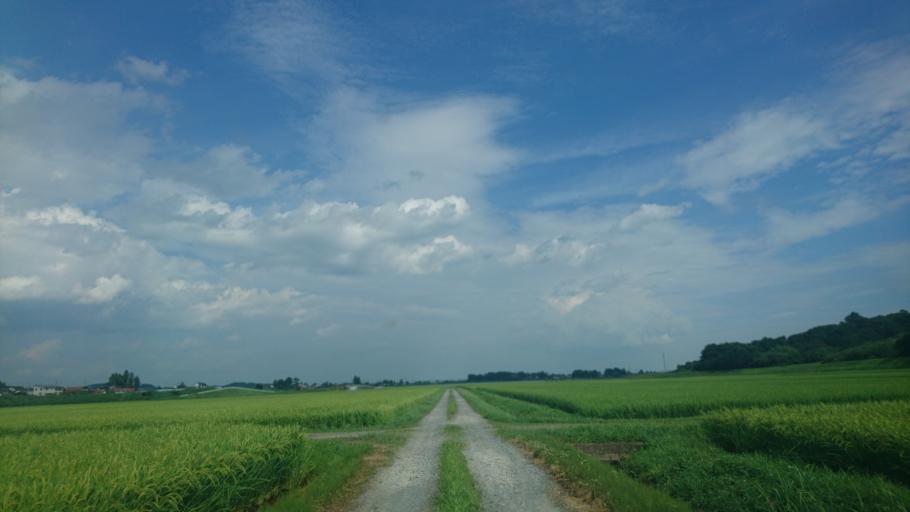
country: JP
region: Iwate
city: Ichinoseki
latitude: 38.7721
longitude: 141.0160
